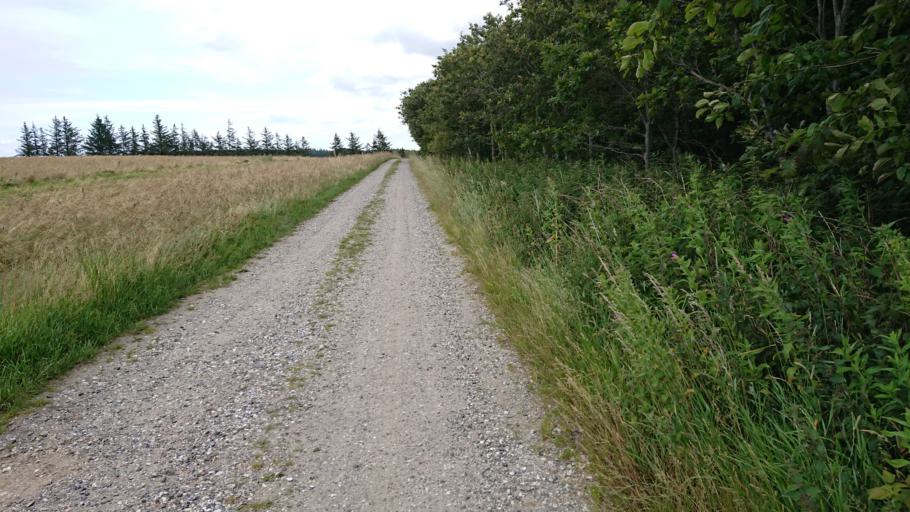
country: DK
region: North Denmark
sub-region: Jammerbugt Kommune
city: Brovst
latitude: 57.1289
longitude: 9.4031
